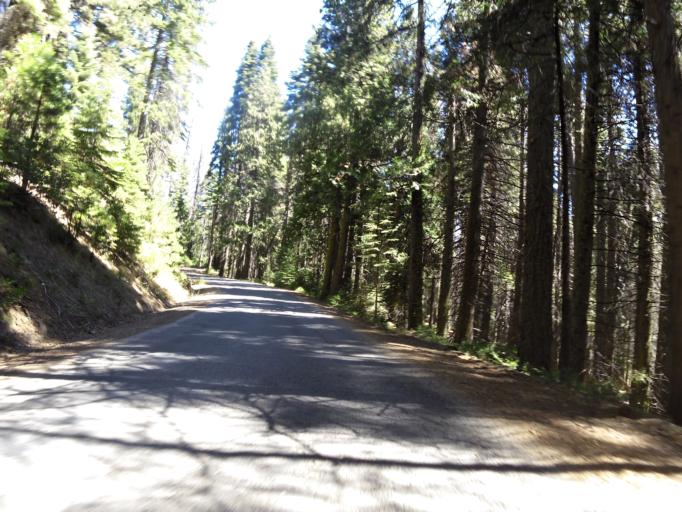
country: US
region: California
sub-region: Madera County
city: Oakhurst
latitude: 37.4318
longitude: -119.5442
